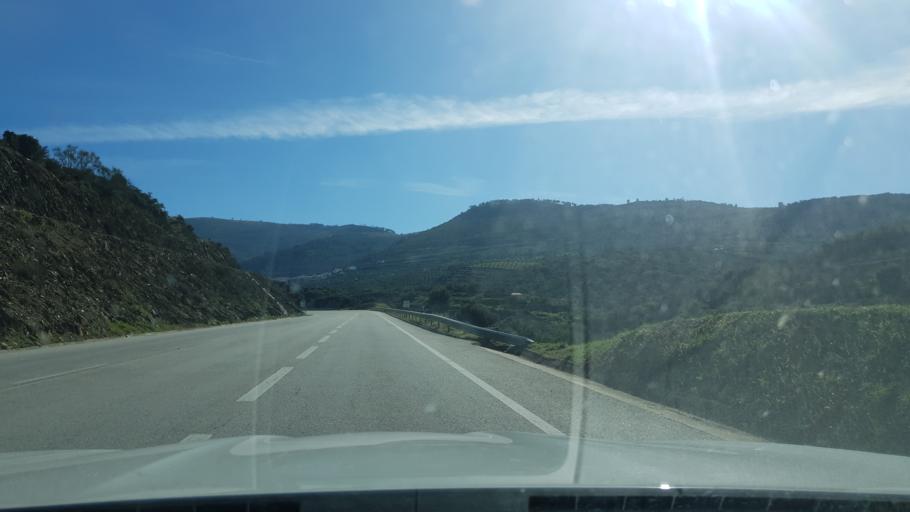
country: PT
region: Braganca
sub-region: Torre de Moncorvo
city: Torre de Moncorvo
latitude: 41.1787
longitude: -7.0742
